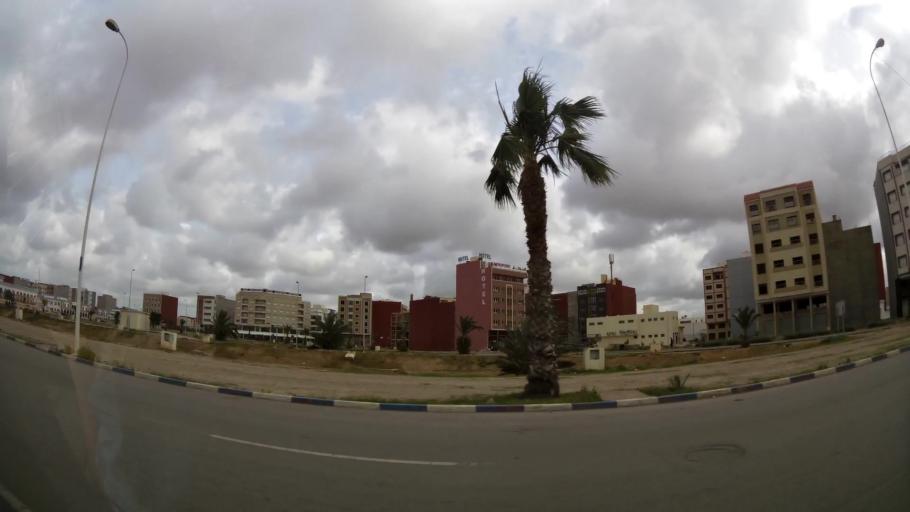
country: MA
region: Oriental
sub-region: Nador
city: Nador
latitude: 35.1527
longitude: -2.9207
